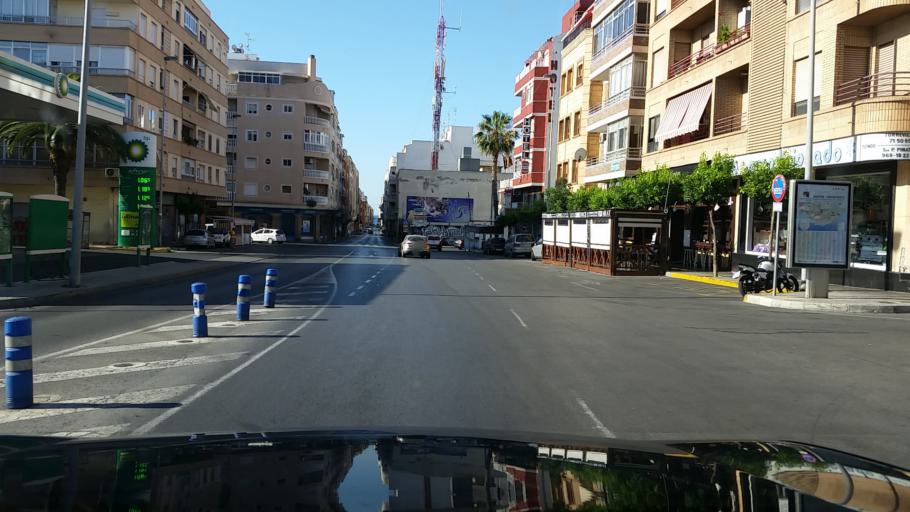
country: ES
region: Valencia
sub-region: Provincia de Alicante
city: Torrevieja
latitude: 37.9833
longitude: -0.6796
